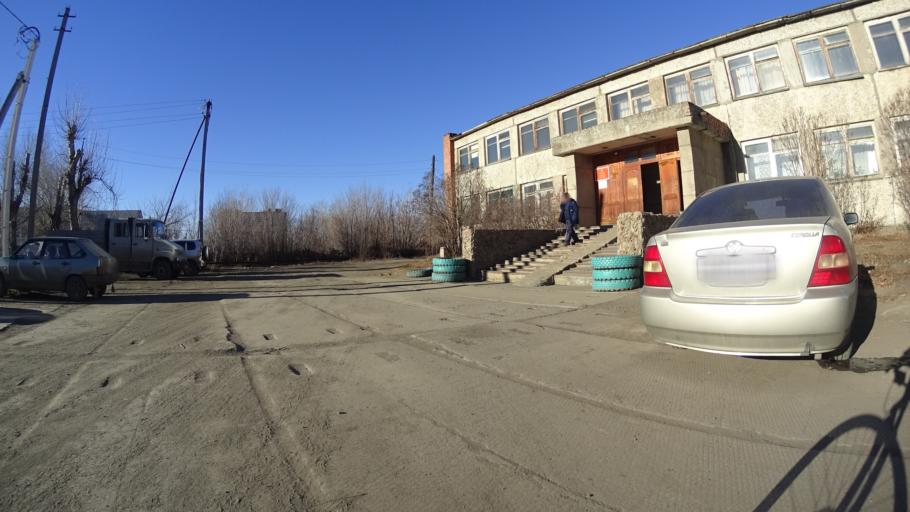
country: RU
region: Chelyabinsk
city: Troitsk
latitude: 54.1093
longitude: 61.5535
